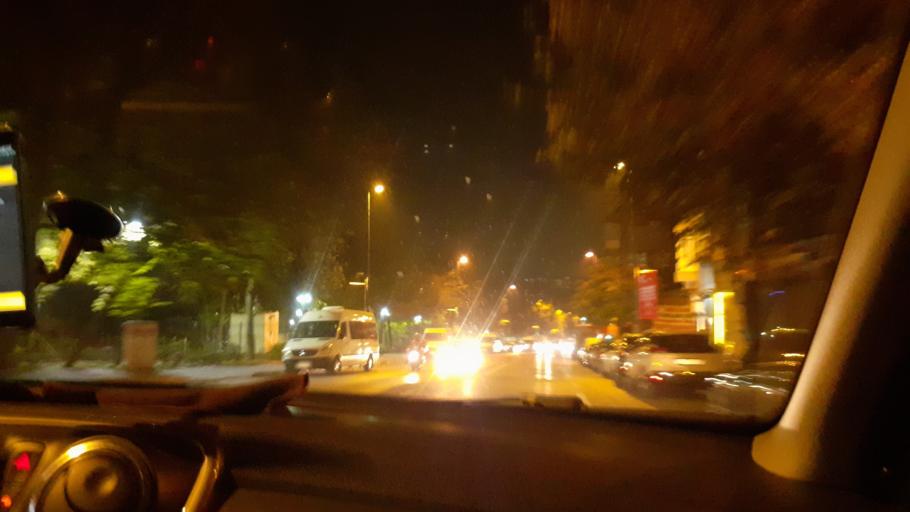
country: TR
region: Istanbul
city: UEskuedar
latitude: 41.0274
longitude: 29.0252
